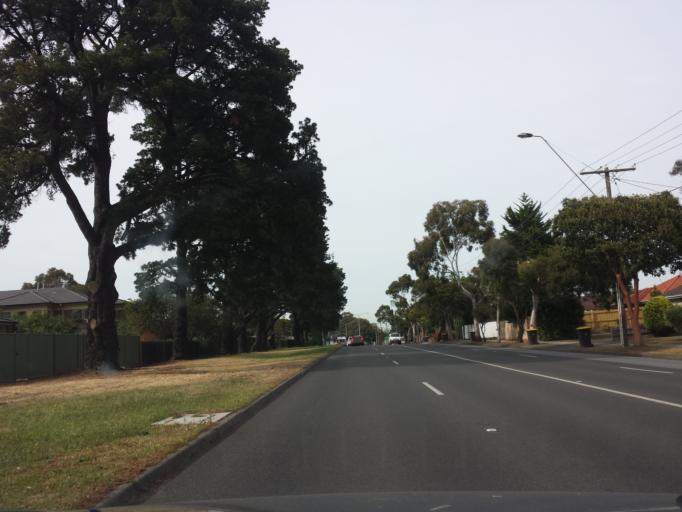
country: AU
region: Victoria
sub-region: Monash
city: Notting Hill
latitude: -37.8966
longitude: 145.1248
